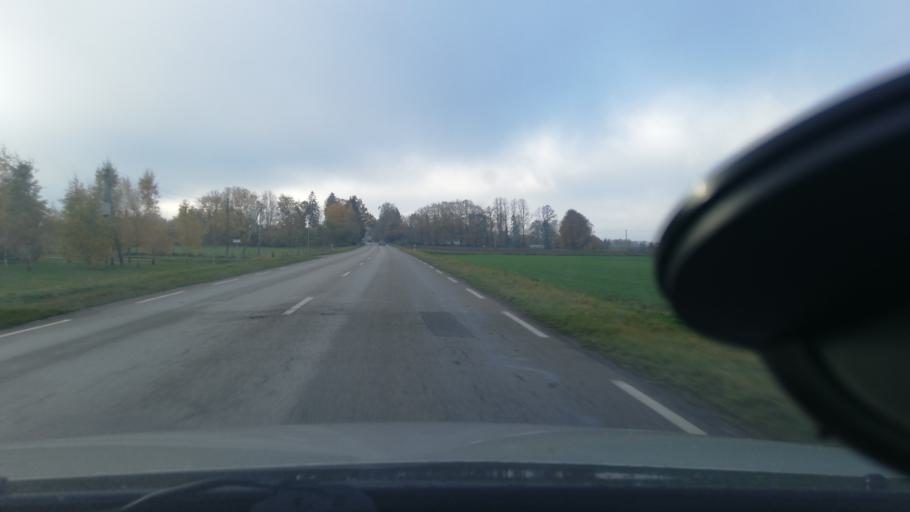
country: LT
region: Klaipedos apskritis
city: Gargzdai
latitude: 55.7505
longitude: 21.3786
